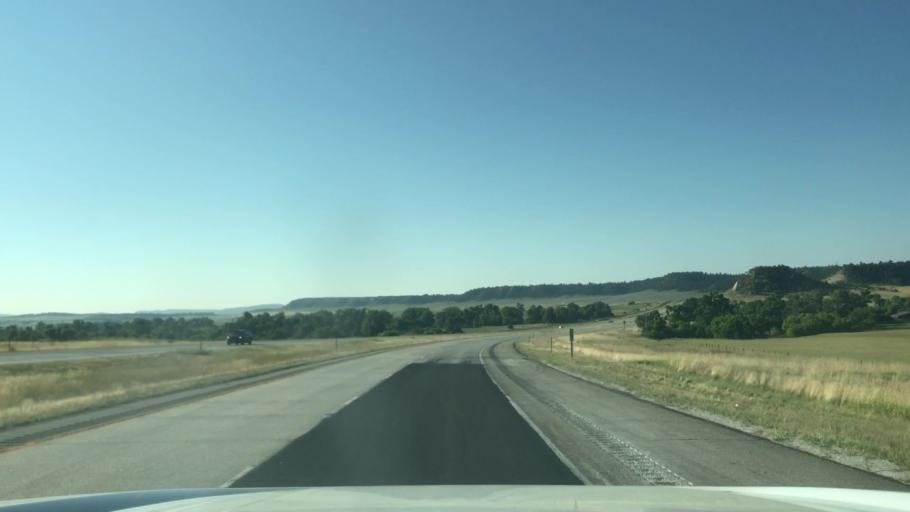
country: US
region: Wyoming
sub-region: Platte County
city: Guernsey
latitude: 42.4799
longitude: -105.0300
